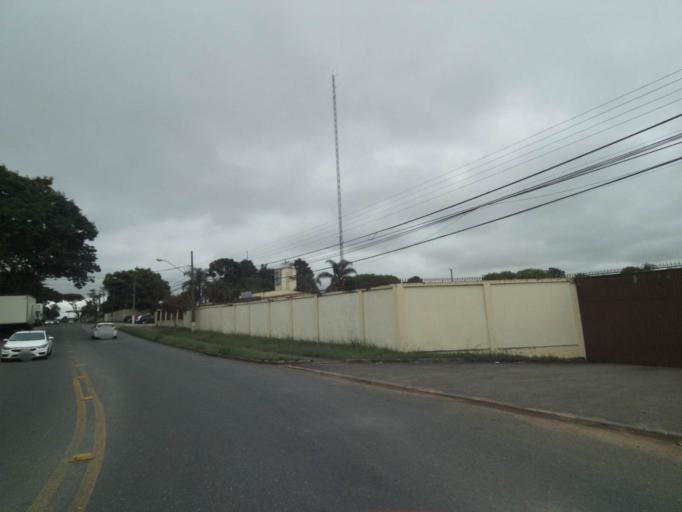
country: BR
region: Parana
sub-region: Curitiba
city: Curitiba
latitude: -25.4844
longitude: -49.2997
